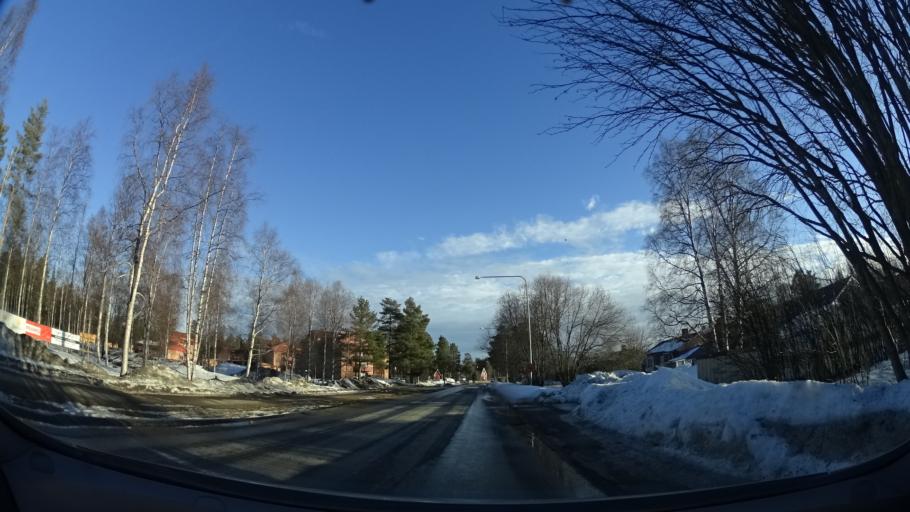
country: SE
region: Vaesterbotten
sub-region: Skelleftea Kommun
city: Byske
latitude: 64.9530
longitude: 21.2143
